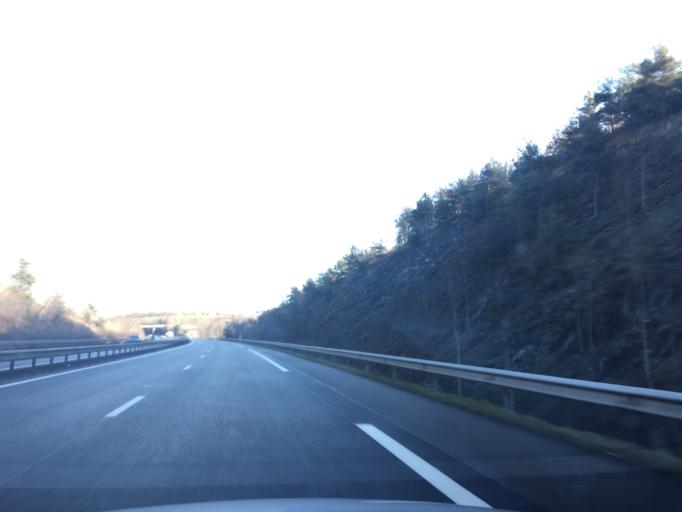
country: FR
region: Rhone-Alpes
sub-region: Departement de la Loire
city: Saint-Germain-Laval
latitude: 45.8586
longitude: 3.9804
